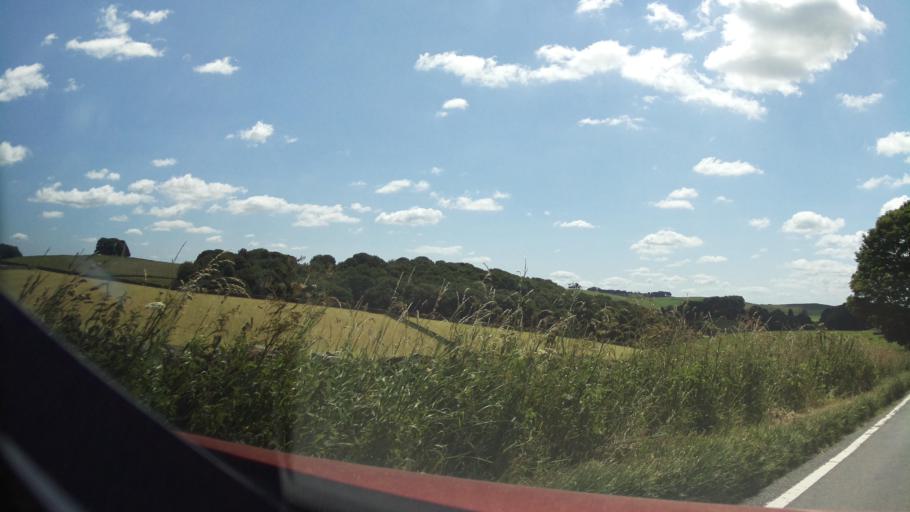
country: GB
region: England
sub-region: Derbyshire
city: Ashbourne
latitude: 53.1027
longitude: -1.7691
